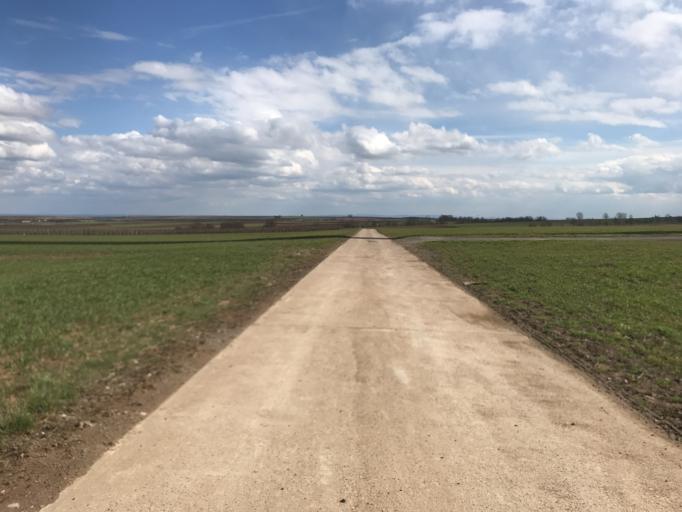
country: DE
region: Rheinland-Pfalz
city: Klein-Winternheim
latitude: 49.9365
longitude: 8.2371
